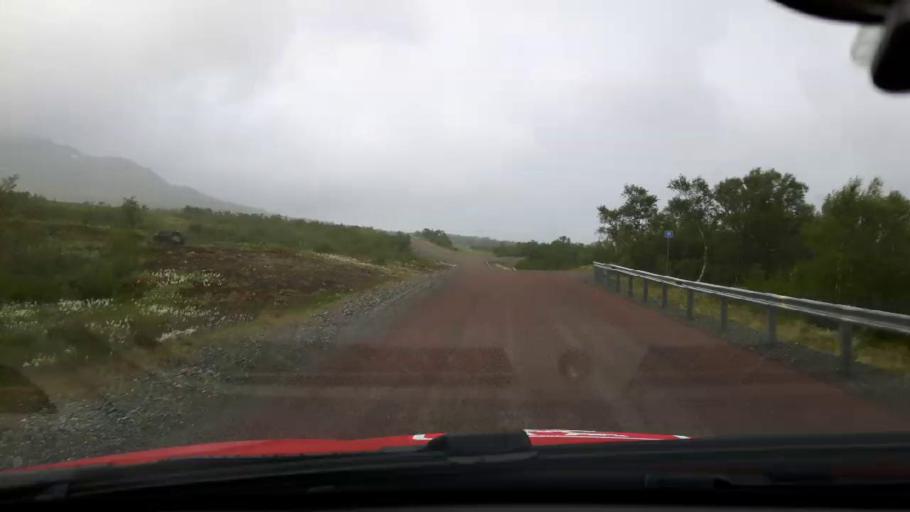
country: NO
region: Nord-Trondelag
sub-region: Meraker
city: Meraker
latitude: 63.1943
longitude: 12.3888
